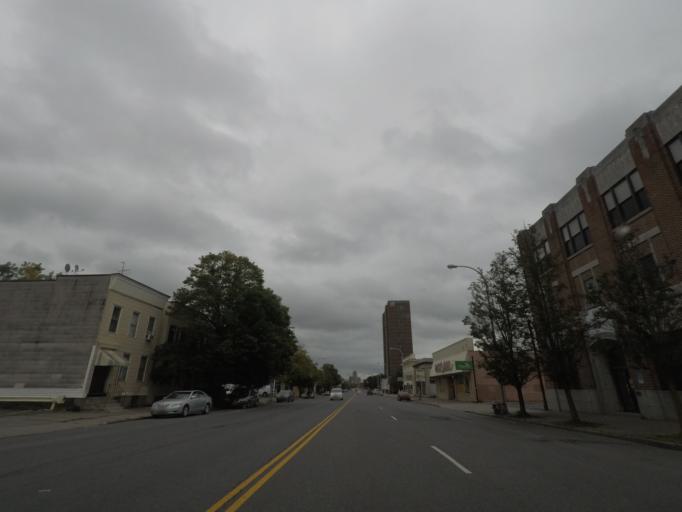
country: US
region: New York
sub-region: Albany County
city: West Albany
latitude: 42.6698
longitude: -73.7783
